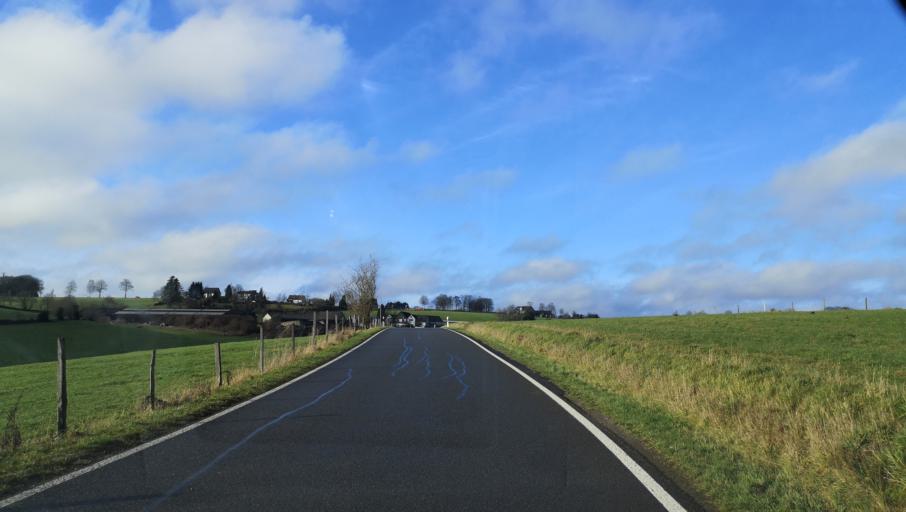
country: DE
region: North Rhine-Westphalia
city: Radevormwald
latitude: 51.1719
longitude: 7.3712
